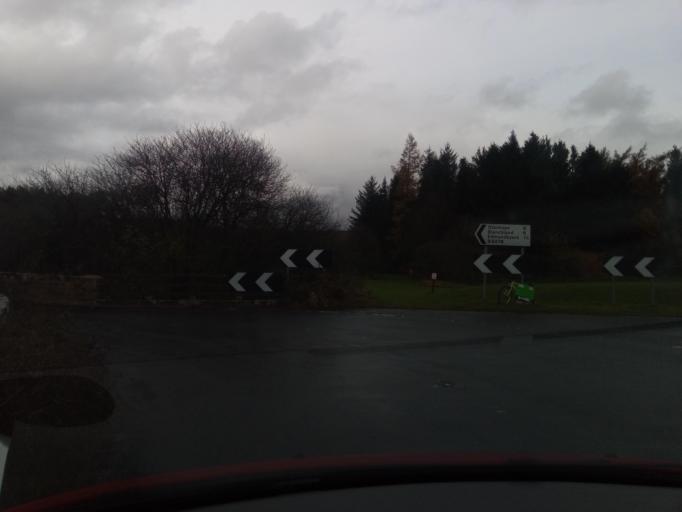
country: GB
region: England
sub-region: County Durham
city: Muggleswick
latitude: 54.8552
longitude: -1.9520
